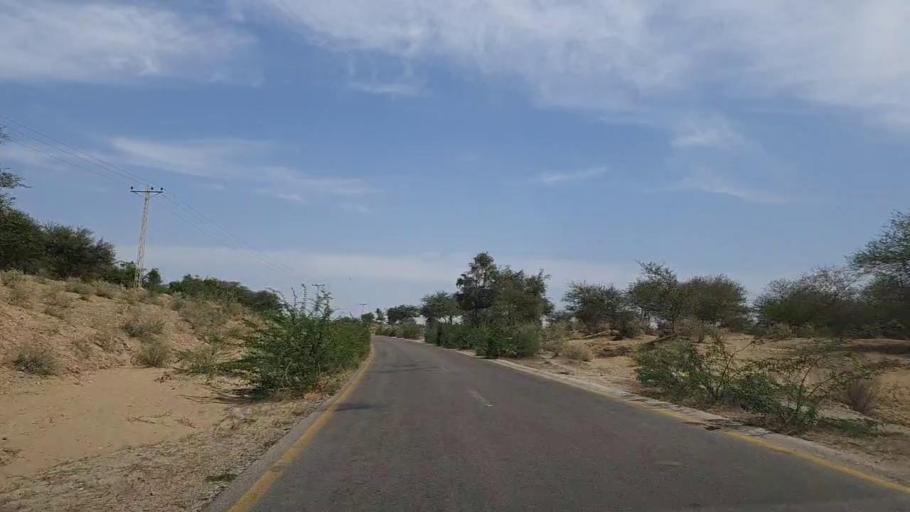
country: PK
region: Sindh
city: Mithi
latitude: 24.7788
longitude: 69.8086
